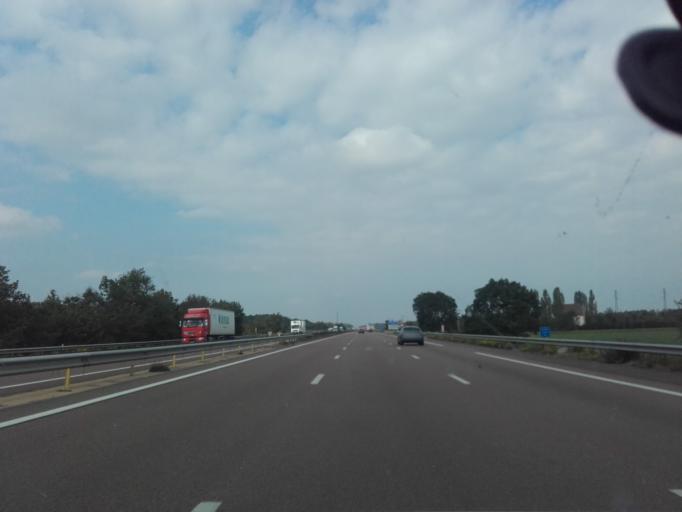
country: FR
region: Bourgogne
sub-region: Departement de Saone-et-Loire
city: Varennes-le-Grand
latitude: 46.6822
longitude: 4.8456
